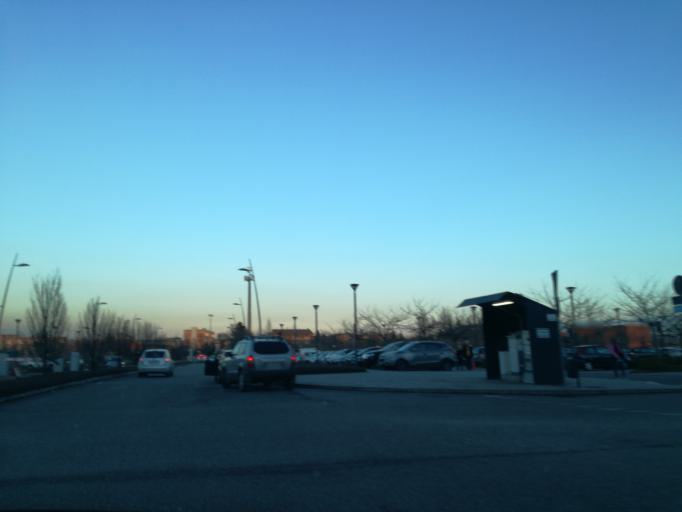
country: IT
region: Lombardy
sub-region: Provincia di Monza e Brianza
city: Vimercate
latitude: 45.6084
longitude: 9.3570
